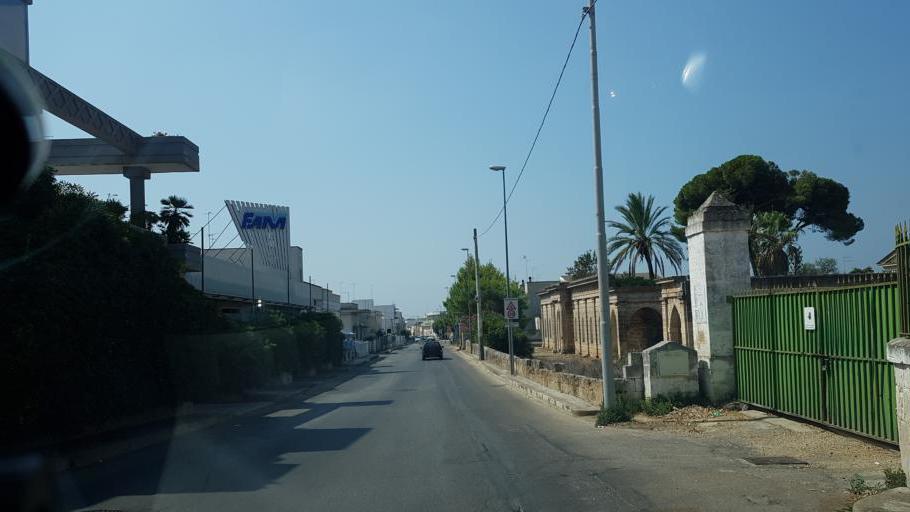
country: IT
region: Apulia
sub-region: Provincia di Taranto
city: Maruggio
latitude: 40.3283
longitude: 17.5739
